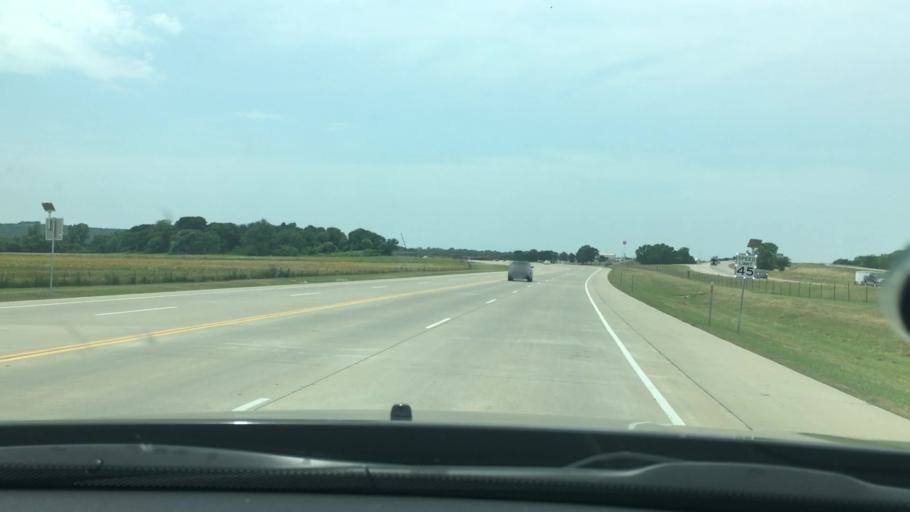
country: US
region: Texas
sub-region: Cooke County
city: Gainesville
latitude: 33.7430
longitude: -97.1395
